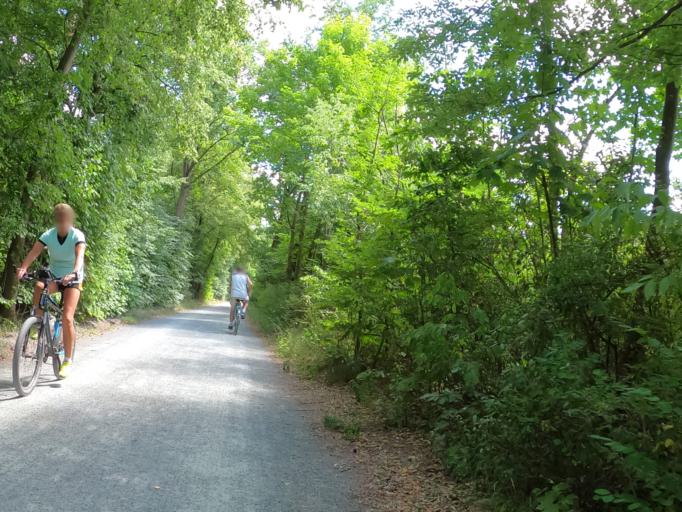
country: DE
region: Hesse
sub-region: Regierungsbezirk Darmstadt
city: Nauheim
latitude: 49.9698
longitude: 8.4638
